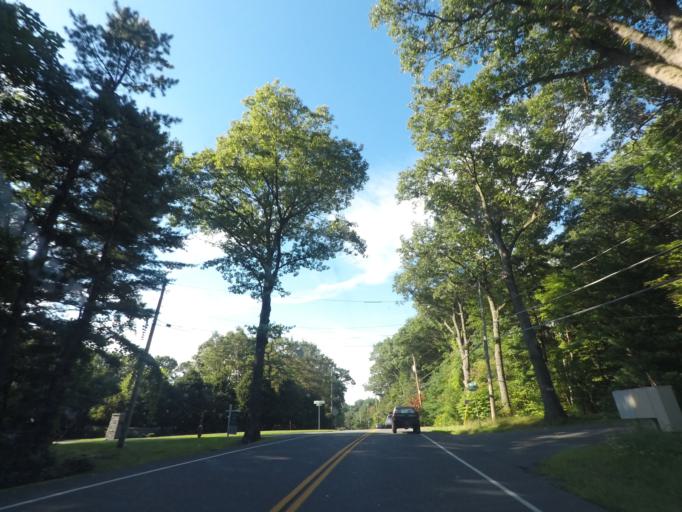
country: US
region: New York
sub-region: Albany County
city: West Albany
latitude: 42.7215
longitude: -73.7713
